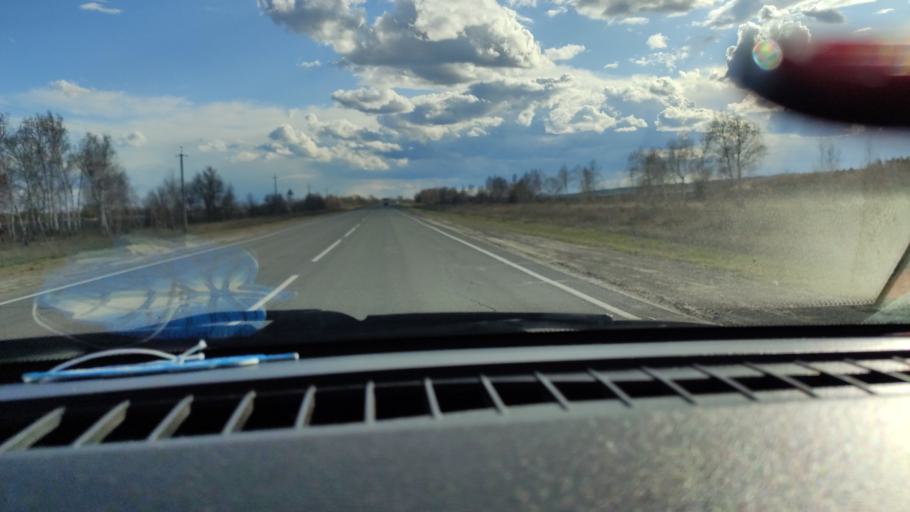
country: RU
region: Saratov
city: Sinodskoye
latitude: 52.0349
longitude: 46.7274
